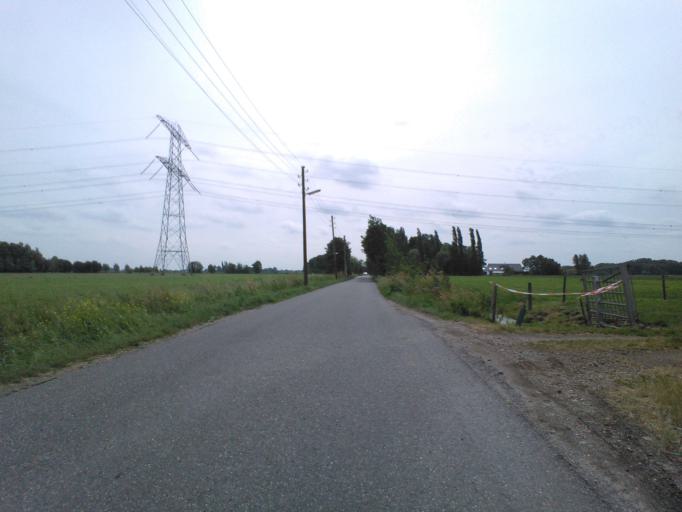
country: NL
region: South Holland
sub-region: Gemeente Gouda
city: Gouda
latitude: 51.9570
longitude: 4.6903
